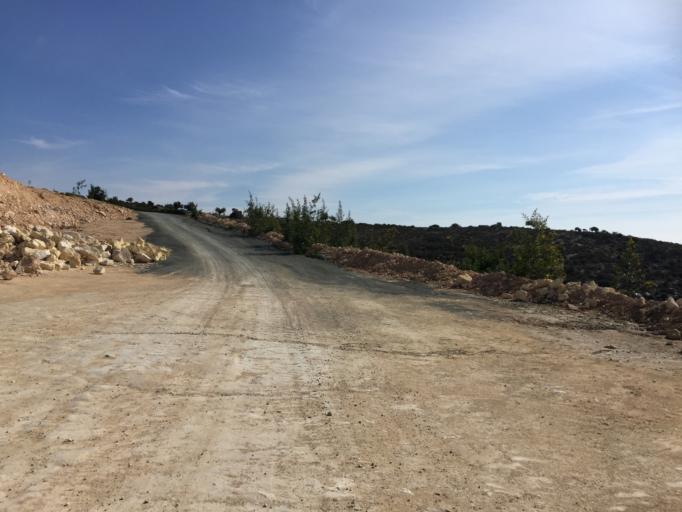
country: CY
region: Larnaka
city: Agios Tychon
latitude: 34.7421
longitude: 33.1203
